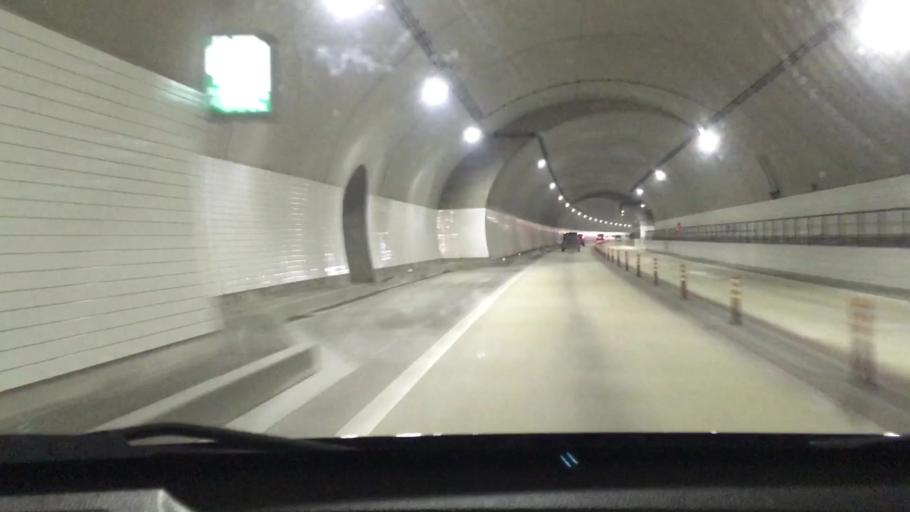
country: JP
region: Saga Prefecture
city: Karatsu
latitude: 33.3673
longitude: 129.9283
